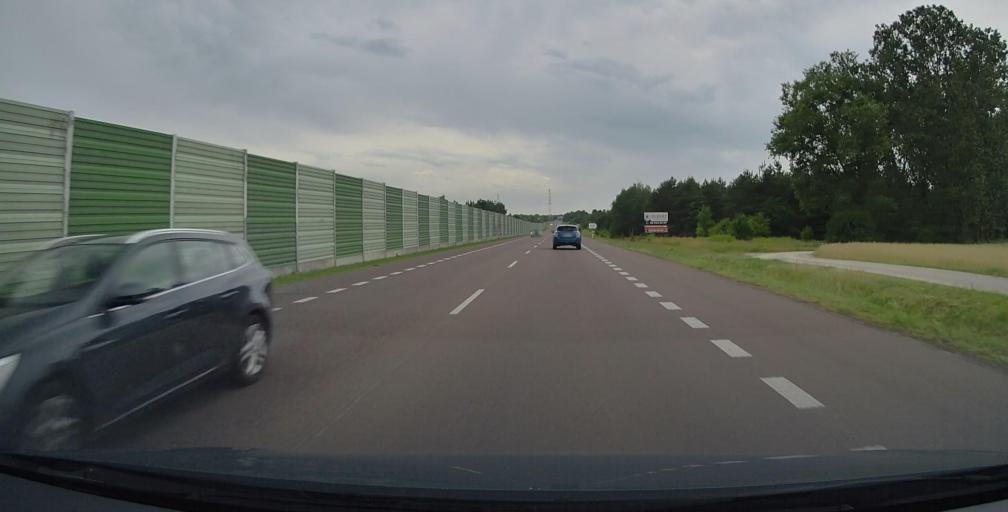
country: PL
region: Lublin Voivodeship
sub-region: Biala Podlaska
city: Biala Podlaska
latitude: 52.0425
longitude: 23.0894
